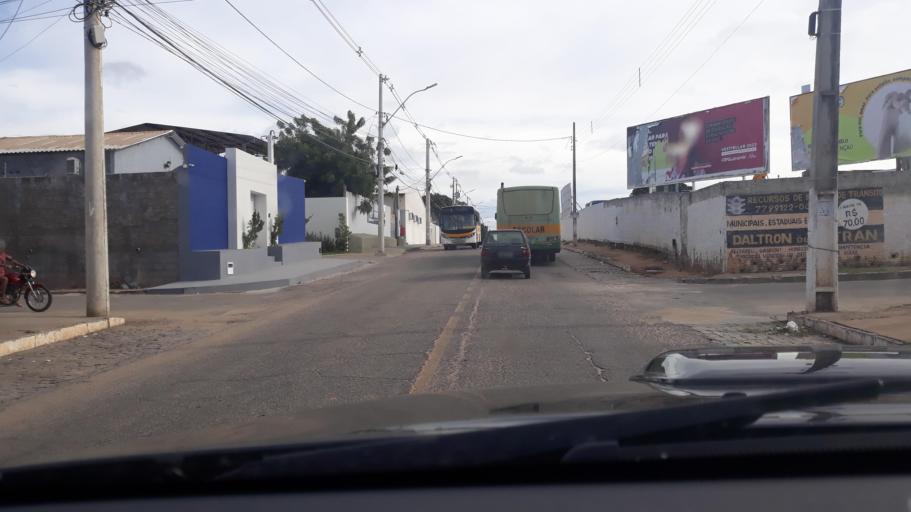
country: BR
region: Bahia
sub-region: Guanambi
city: Guanambi
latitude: -14.2139
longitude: -42.7715
